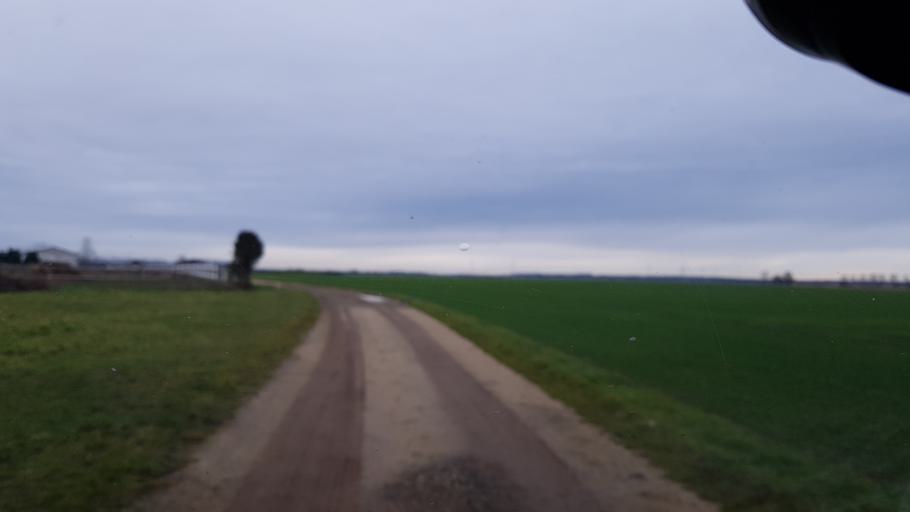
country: DE
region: Brandenburg
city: Doberlug-Kirchhain
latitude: 51.6530
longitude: 13.5479
